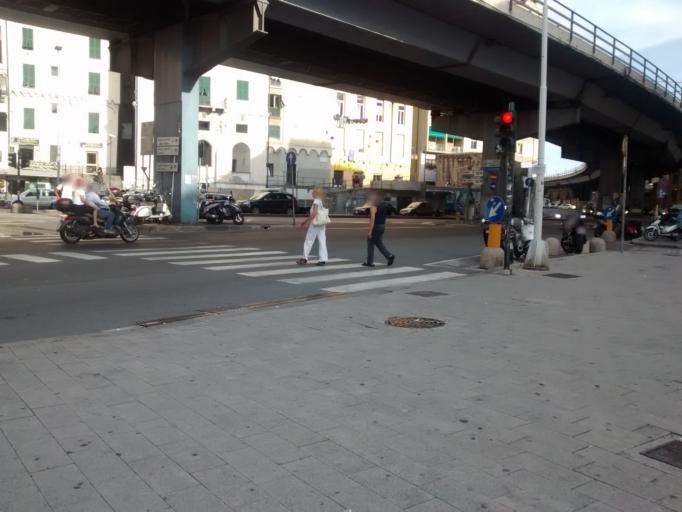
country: IT
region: Liguria
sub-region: Provincia di Genova
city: San Teodoro
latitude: 44.4069
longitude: 8.9273
